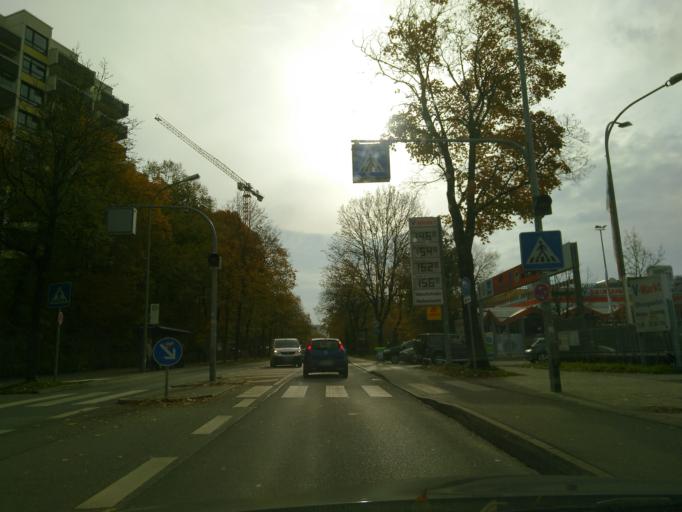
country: DE
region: Bavaria
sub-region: Upper Bavaria
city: Munich
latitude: 48.1215
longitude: 11.5989
